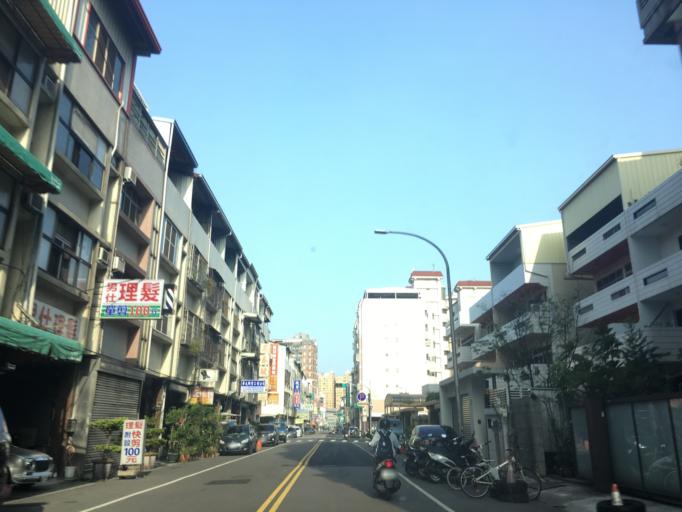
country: TW
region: Taiwan
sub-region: Taichung City
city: Taichung
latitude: 24.1685
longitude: 120.6809
